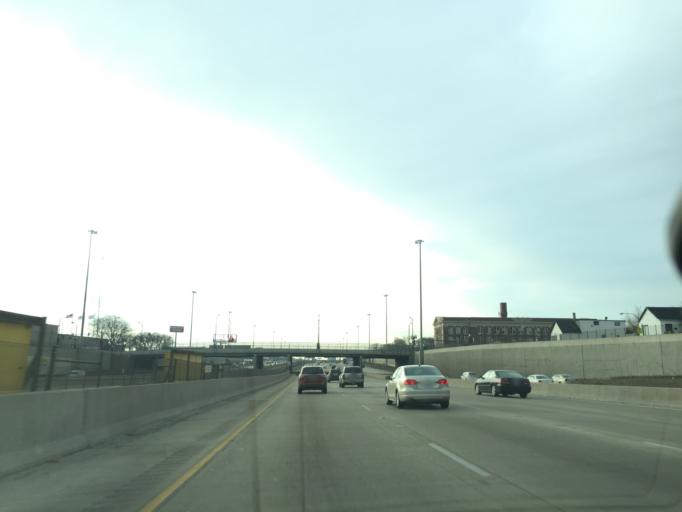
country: US
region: Illinois
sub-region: Cook County
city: Chicago
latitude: 41.8036
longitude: -87.6316
